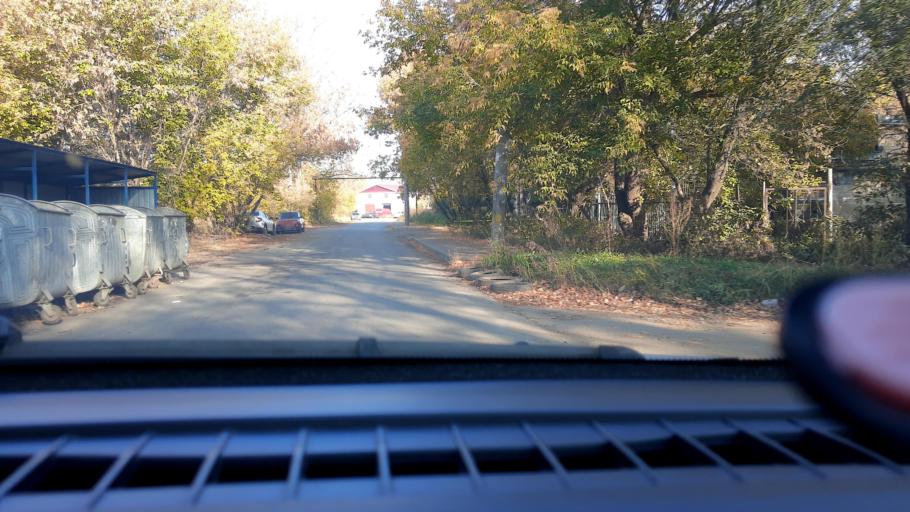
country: RU
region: Nizjnij Novgorod
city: Nizhniy Novgorod
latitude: 56.3038
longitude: 43.8808
